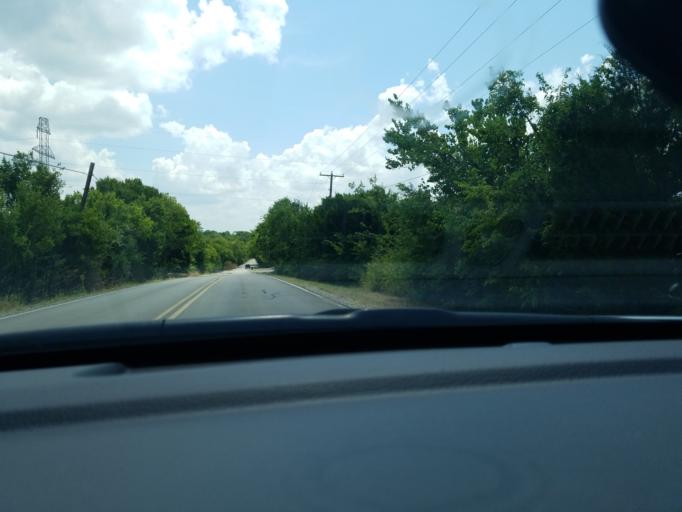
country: US
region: Texas
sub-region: Dallas County
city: Sunnyvale
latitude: 32.8140
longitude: -96.5812
